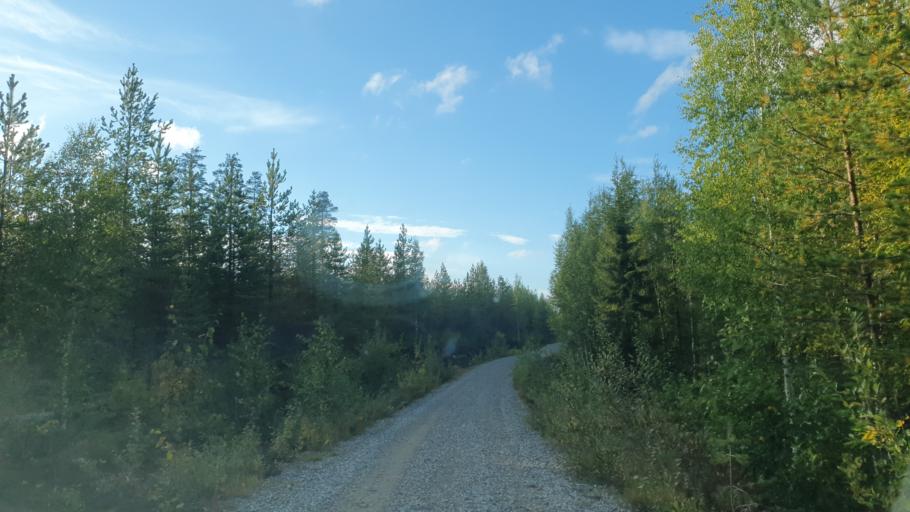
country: FI
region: Kainuu
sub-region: Kehys-Kainuu
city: Kuhmo
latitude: 64.3318
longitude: 30.0130
